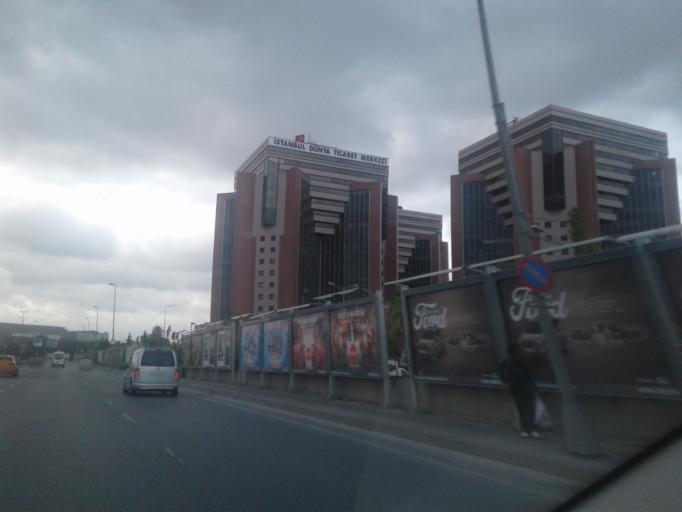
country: TR
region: Istanbul
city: Bahcelievler
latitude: 40.9842
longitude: 28.8327
